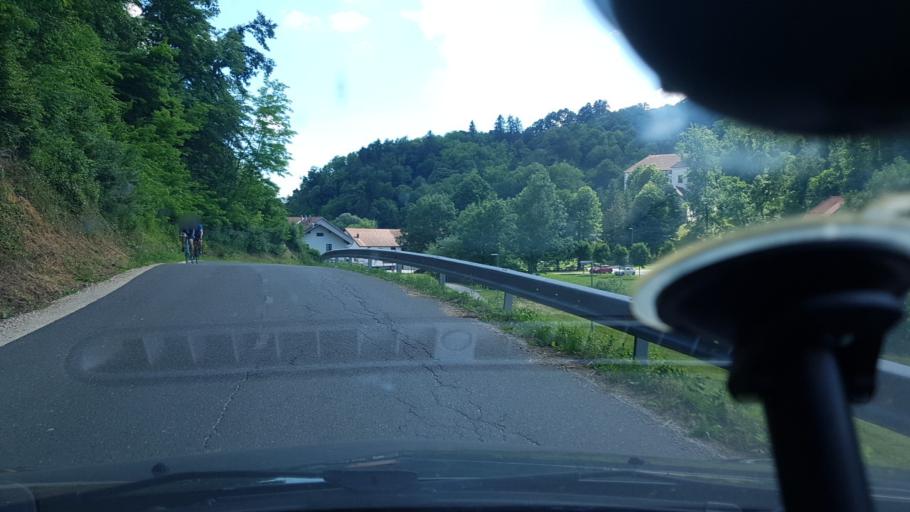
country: SI
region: Rogatec
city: Rogatec
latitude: 46.2311
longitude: 15.6990
